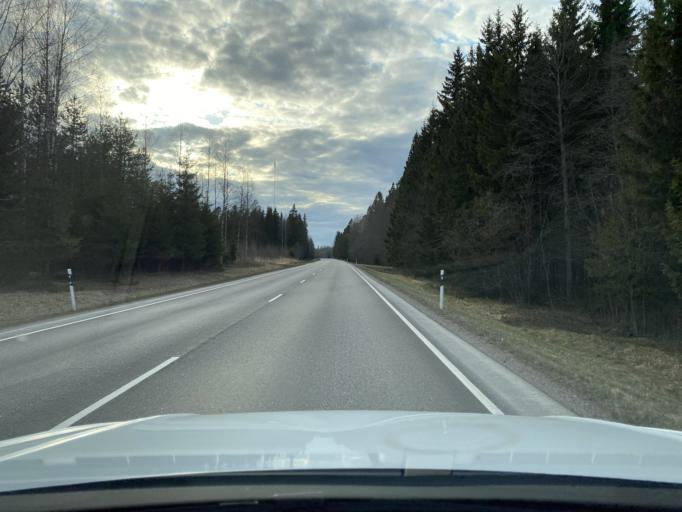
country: FI
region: Haeme
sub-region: Haemeenlinna
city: Renko
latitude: 60.7850
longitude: 24.1466
